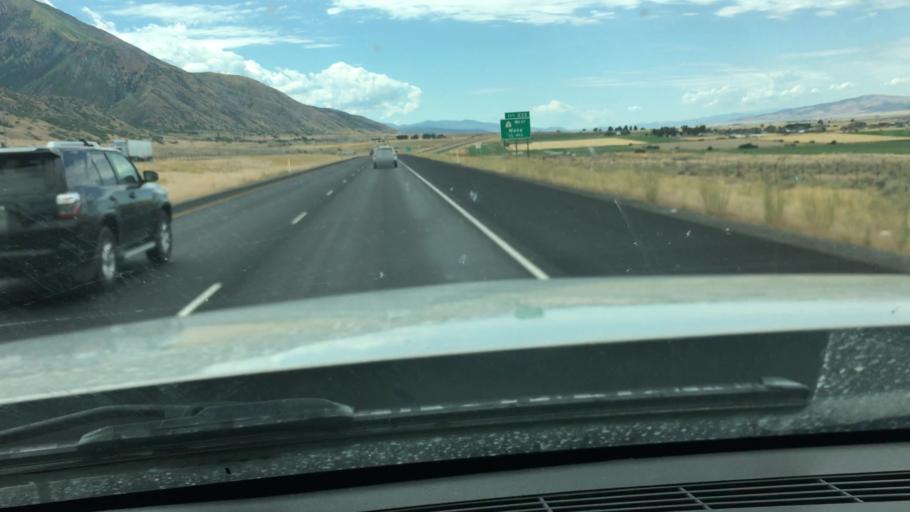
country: US
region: Utah
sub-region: Juab County
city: Mona
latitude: 39.8303
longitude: -111.8343
